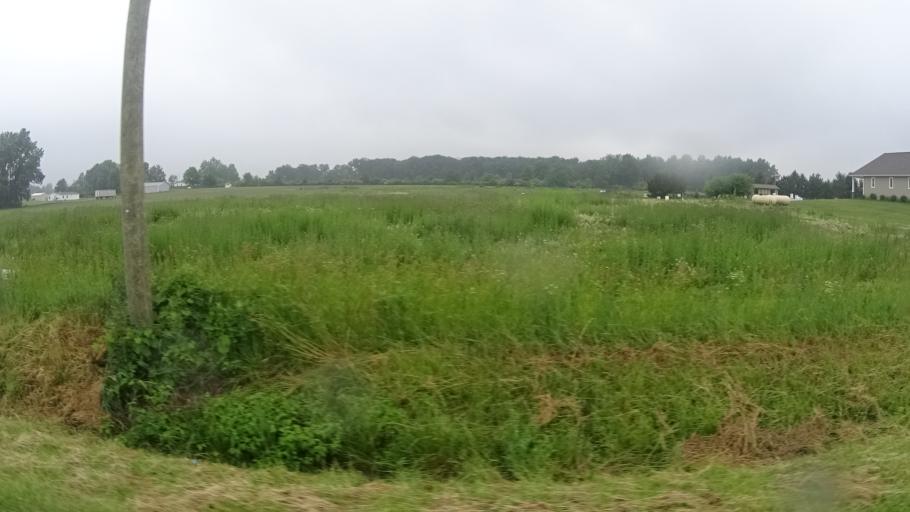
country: US
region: Ohio
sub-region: Huron County
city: Bellevue
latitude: 41.3157
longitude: -82.8426
